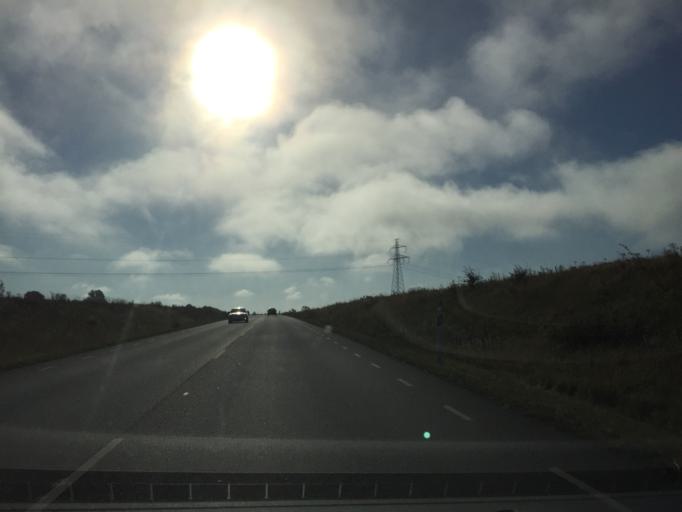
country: SE
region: Skane
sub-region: Staffanstorps Kommun
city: Hjaerup
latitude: 55.6844
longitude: 13.1592
